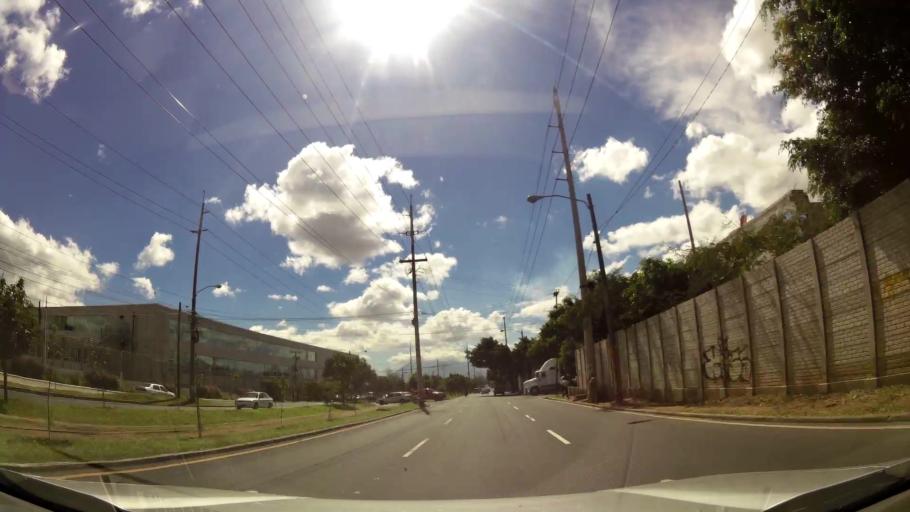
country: GT
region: Guatemala
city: Santa Catarina Pinula
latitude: 14.5672
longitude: -90.5443
